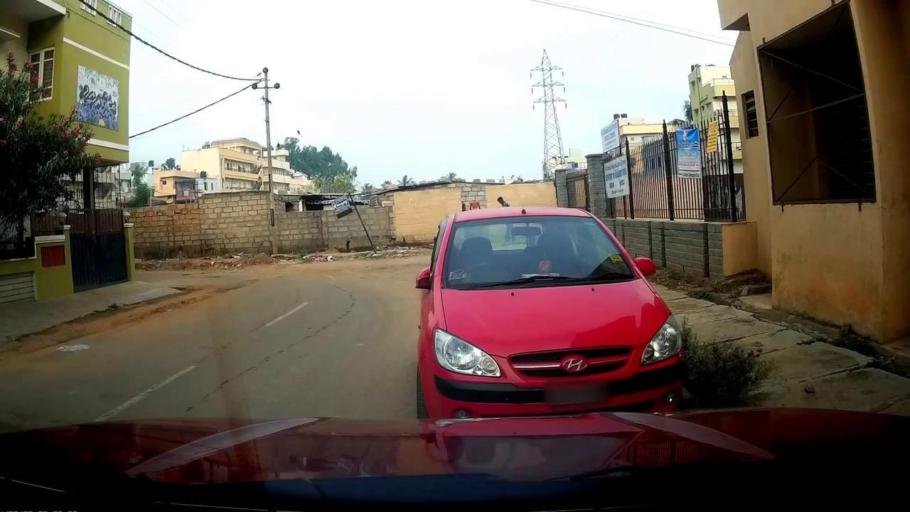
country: IN
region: Karnataka
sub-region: Bangalore Urban
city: Bangalore
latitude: 13.0359
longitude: 77.5660
